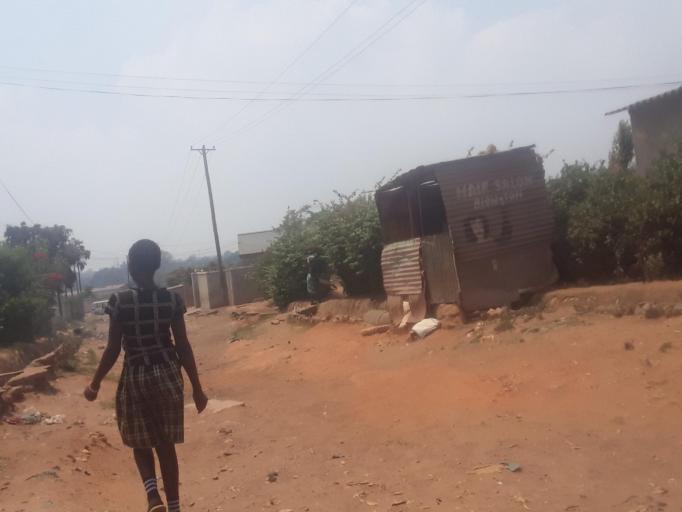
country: ZM
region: Lusaka
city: Lusaka
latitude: -15.3676
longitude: 28.2959
